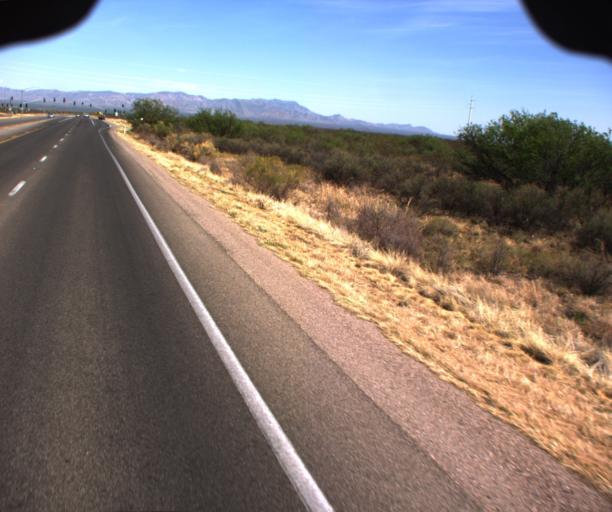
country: US
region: Arizona
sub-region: Cochise County
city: Sierra Vista Southeast
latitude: 31.5521
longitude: -110.1927
